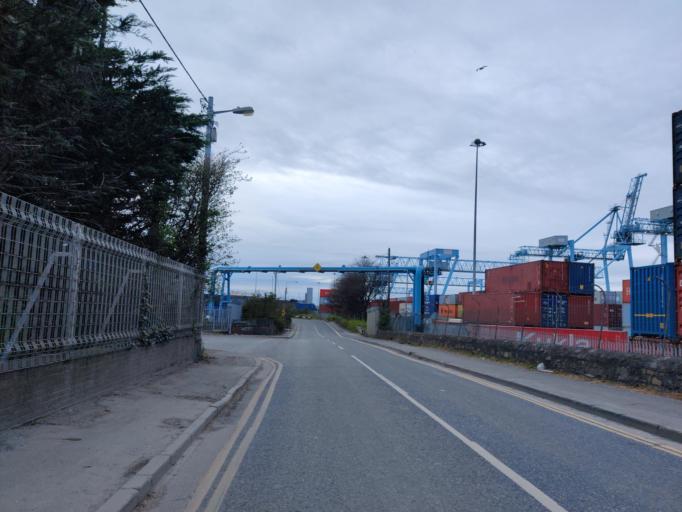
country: IE
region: Leinster
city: Sandymount
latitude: 53.3414
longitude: -6.2059
